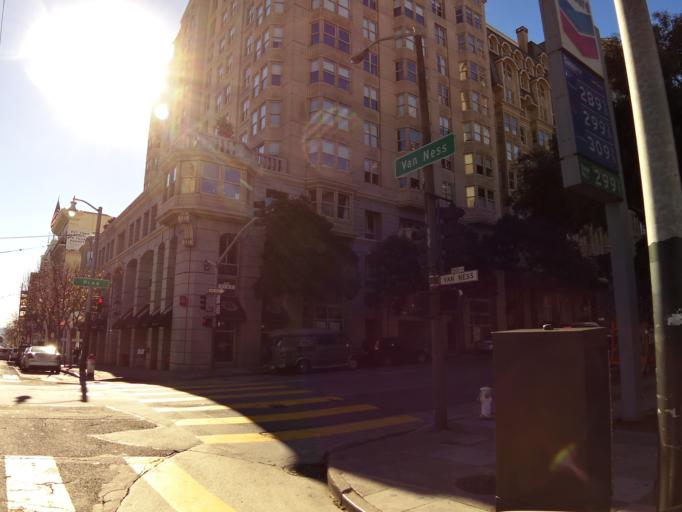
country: US
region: California
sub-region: San Francisco County
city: San Francisco
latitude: 37.7895
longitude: -122.4223
